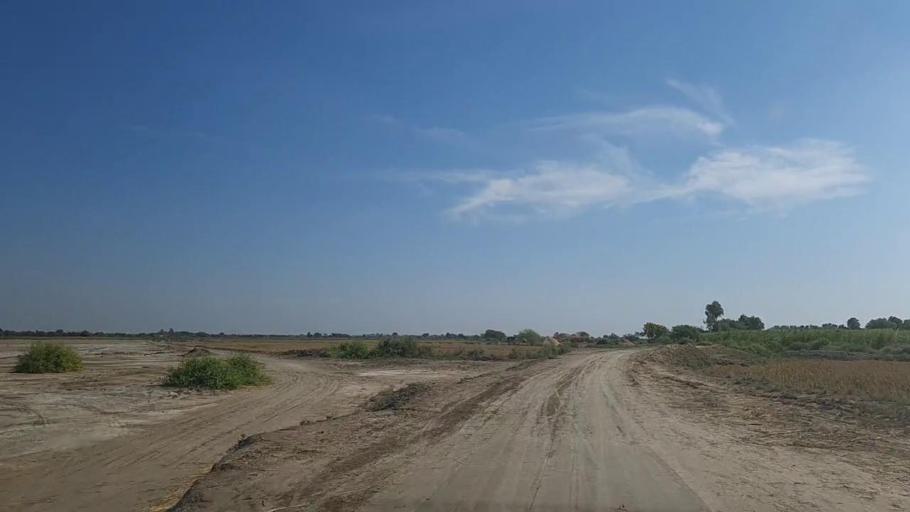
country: PK
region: Sindh
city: Mirpur Batoro
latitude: 24.7610
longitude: 68.2964
